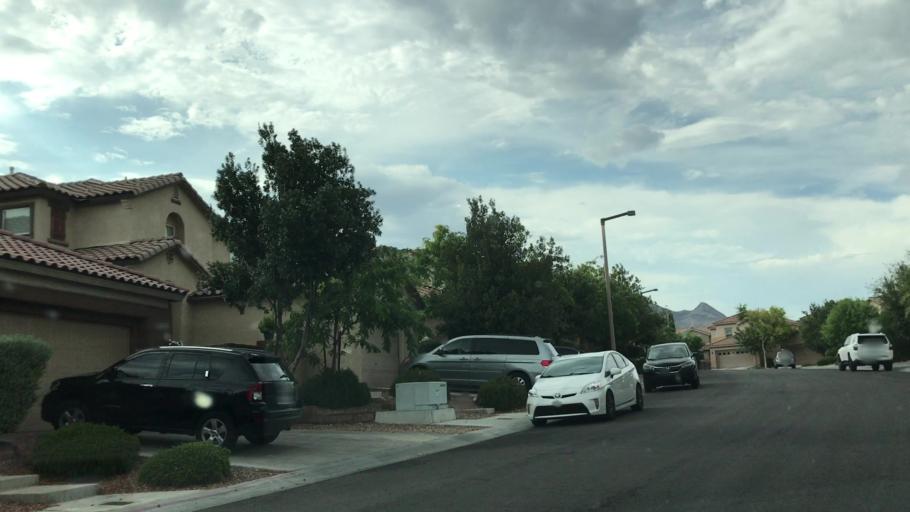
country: US
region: Nevada
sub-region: Clark County
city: Summerlin South
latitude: 36.1665
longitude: -115.3506
